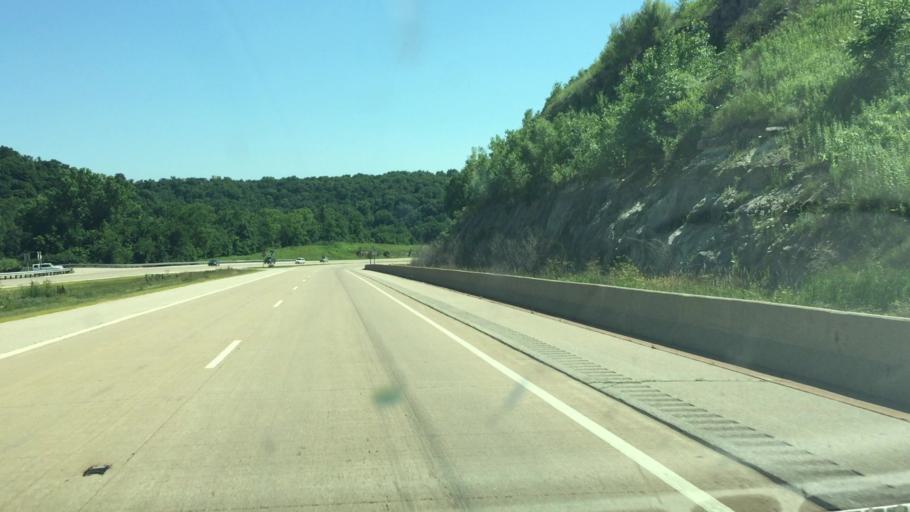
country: US
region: Wisconsin
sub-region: Grant County
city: Dickeyville
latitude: 42.6662
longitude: -90.5506
